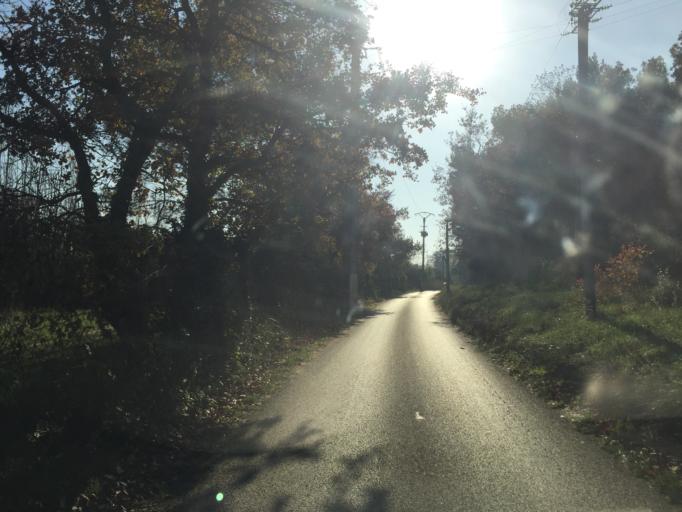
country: FR
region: Provence-Alpes-Cote d'Azur
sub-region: Departement du Vaucluse
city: Entraigues-sur-la-Sorgue
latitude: 44.0162
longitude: 4.9099
